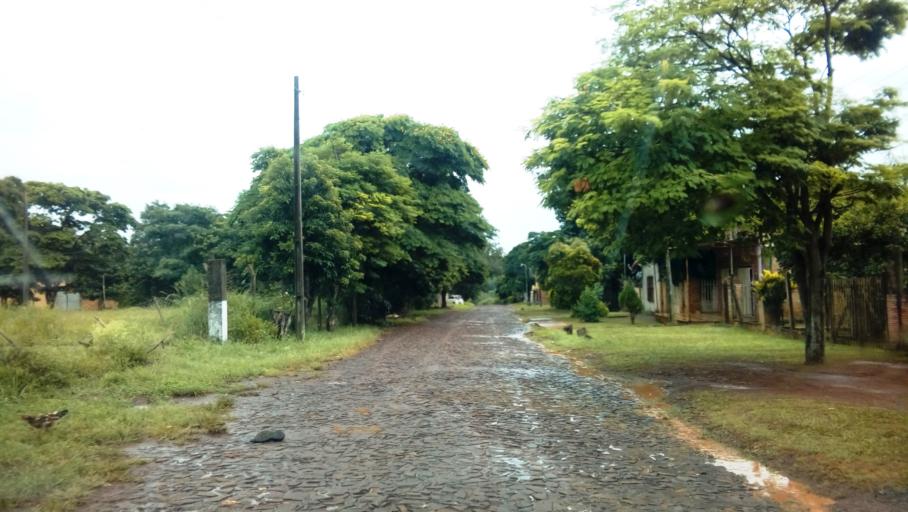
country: PY
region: Alto Parana
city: Ciudad del Este
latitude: -25.4197
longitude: -54.6388
